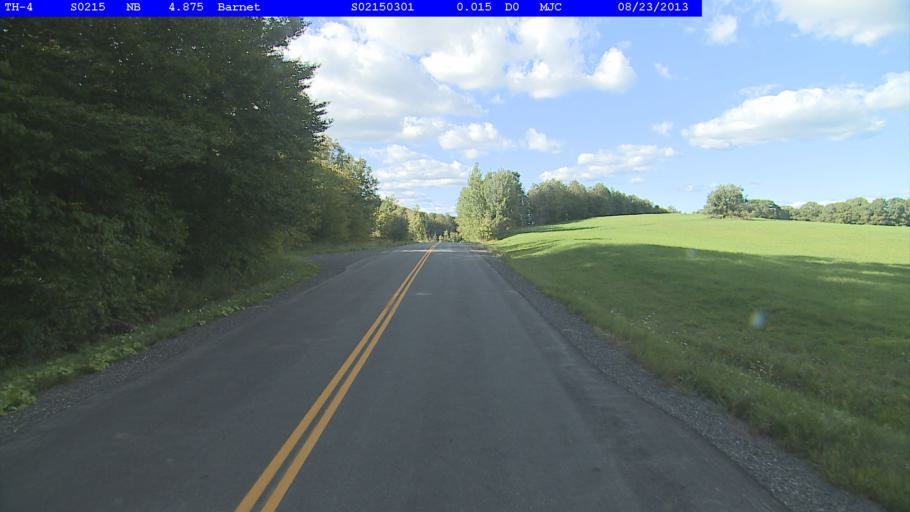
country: US
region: New Hampshire
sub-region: Grafton County
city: Woodsville
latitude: 44.2745
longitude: -72.1737
